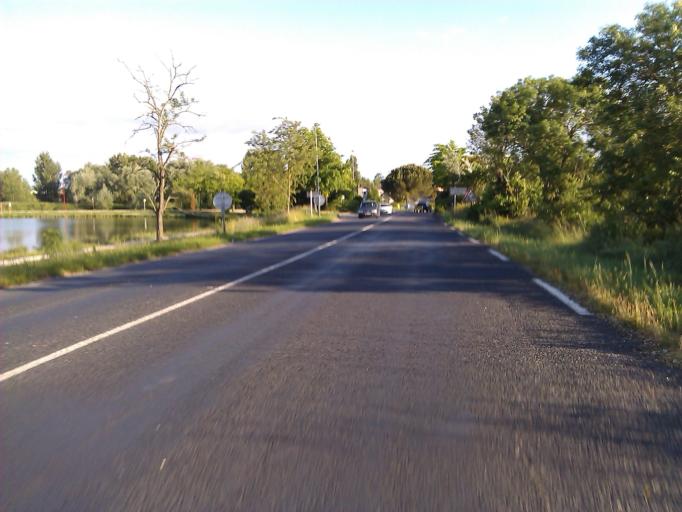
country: FR
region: Aquitaine
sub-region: Departement de la Gironde
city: Saint-Vincent-de-Paul
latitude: 44.9573
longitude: -0.4686
